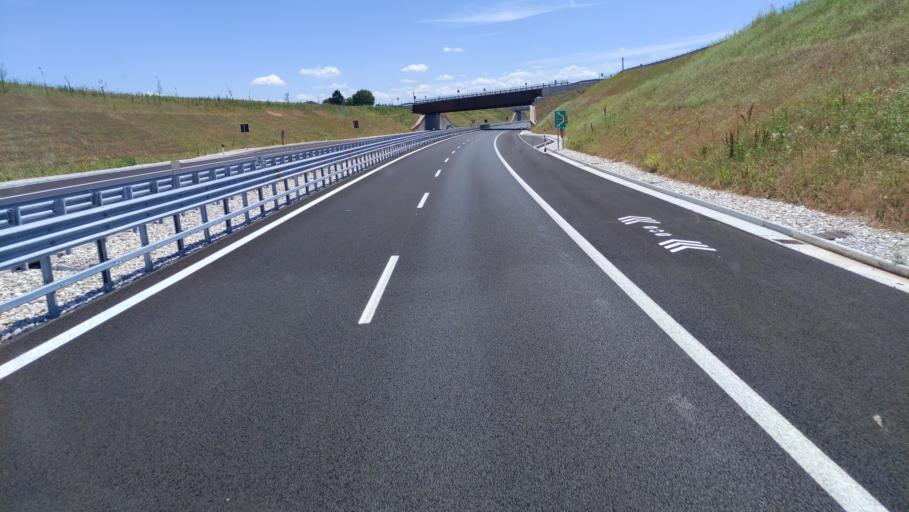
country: IT
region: Veneto
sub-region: Provincia di Treviso
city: Altivole
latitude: 45.7397
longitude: 11.9449
